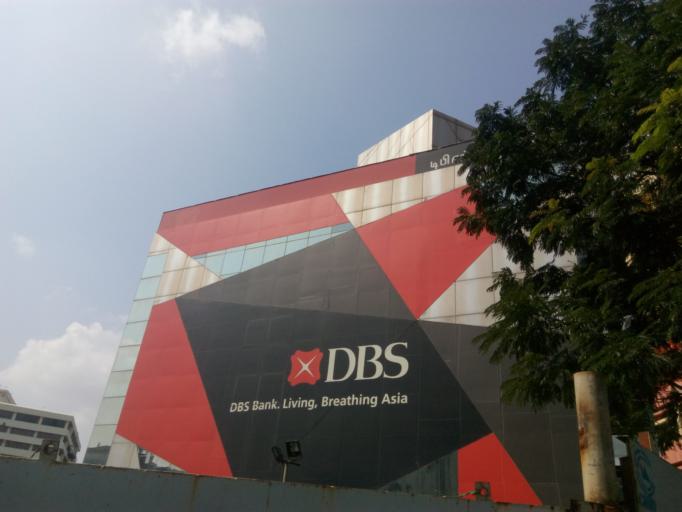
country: IN
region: Tamil Nadu
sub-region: Chennai
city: Chetput
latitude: 13.0642
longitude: 80.2660
